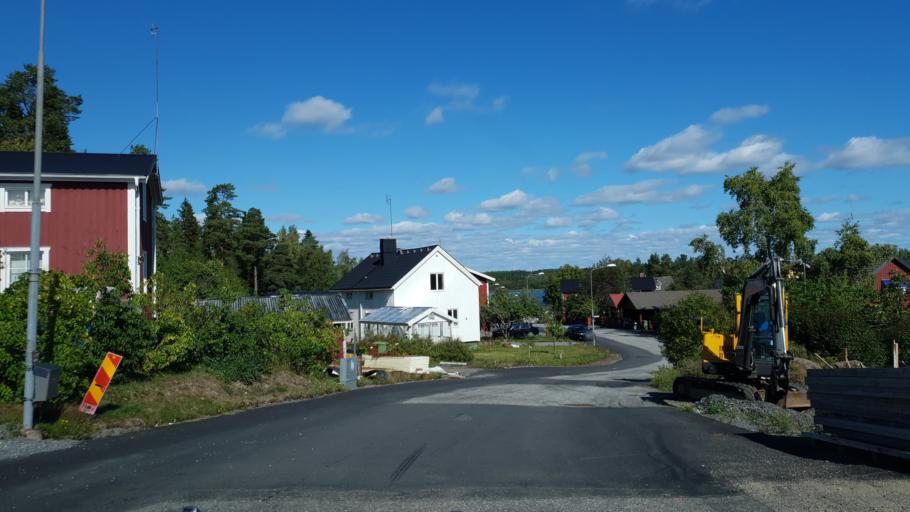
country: SE
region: Vaesterbotten
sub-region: Umea Kommun
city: Holmsund
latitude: 63.7168
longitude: 20.3811
